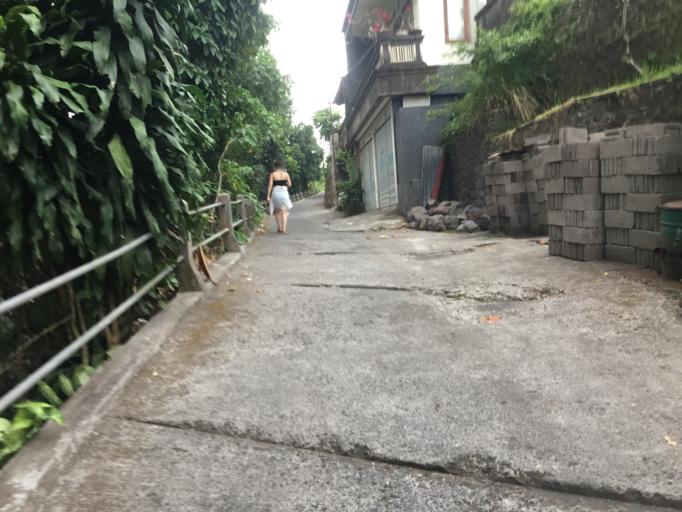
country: ID
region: Bali
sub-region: Kabupaten Gianyar
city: Ubud
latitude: -8.5048
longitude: 115.2563
